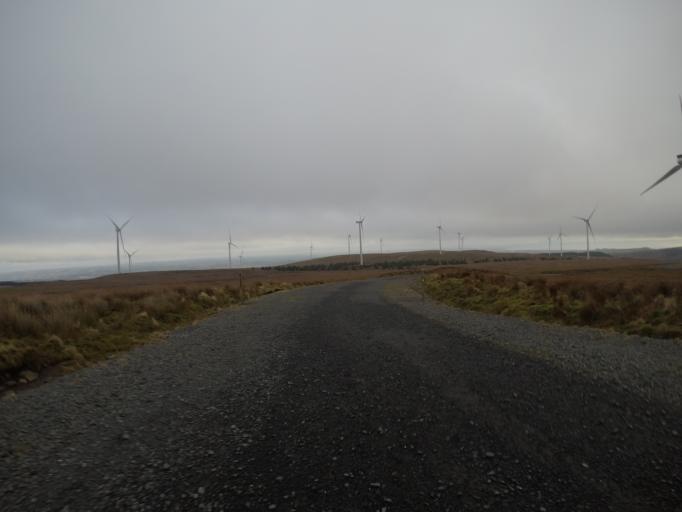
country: GB
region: Scotland
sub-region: North Ayrshire
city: Fairlie
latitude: 55.7424
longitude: -4.7906
